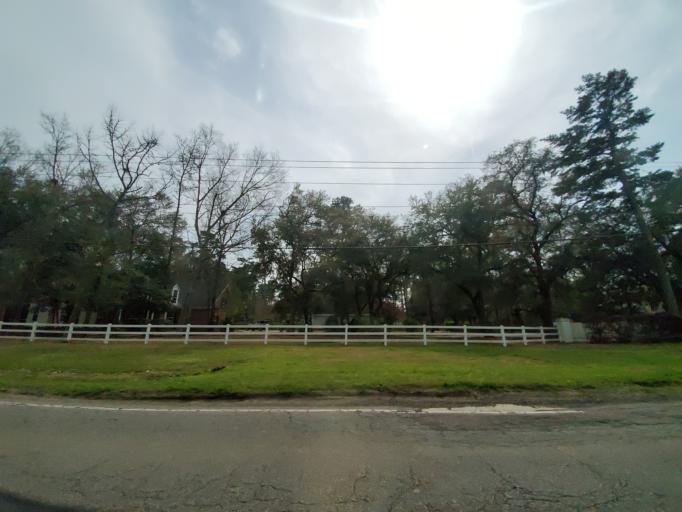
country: US
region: South Carolina
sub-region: Dorchester County
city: Centerville
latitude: 32.9487
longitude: -80.2293
